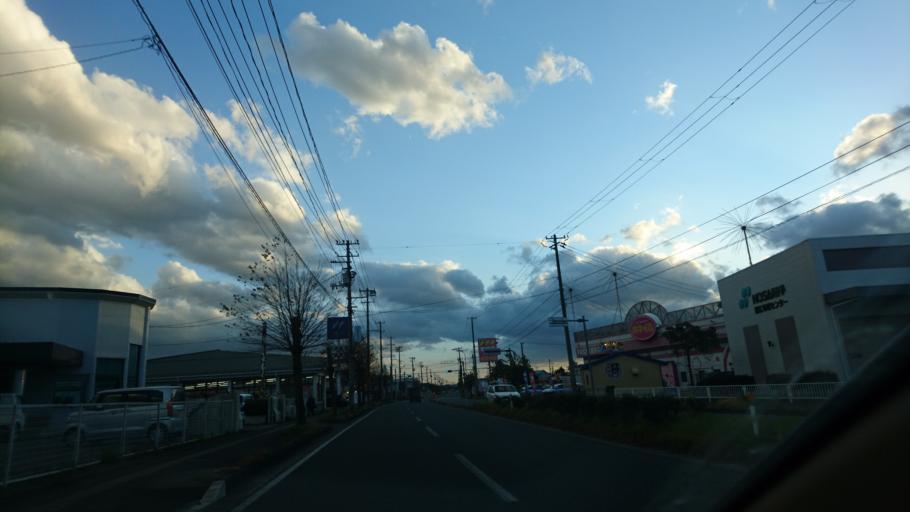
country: JP
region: Iwate
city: Mizusawa
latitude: 39.1534
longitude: 141.1338
